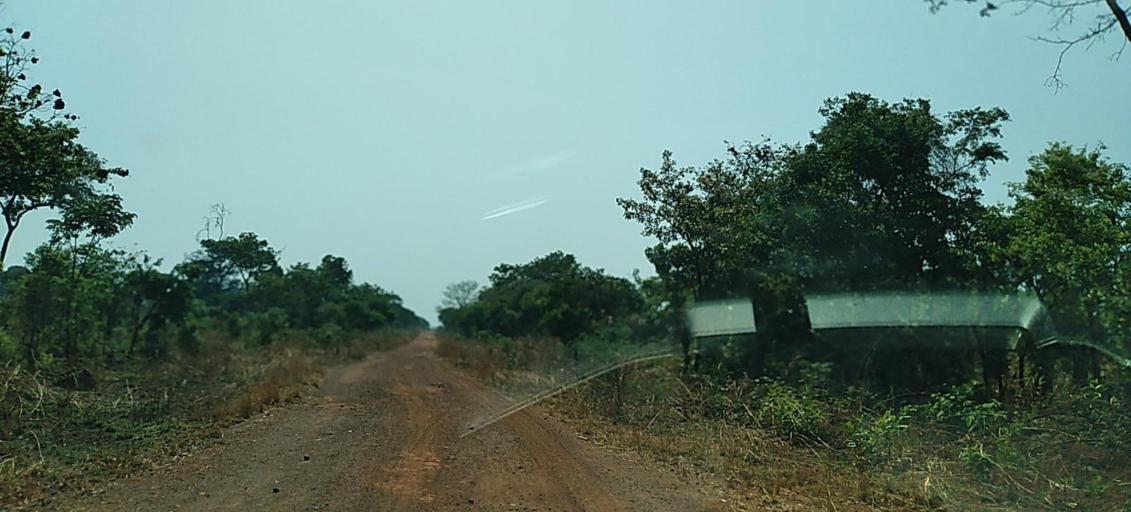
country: ZM
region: North-Western
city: Kansanshi
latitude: -12.0075
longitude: 26.5204
